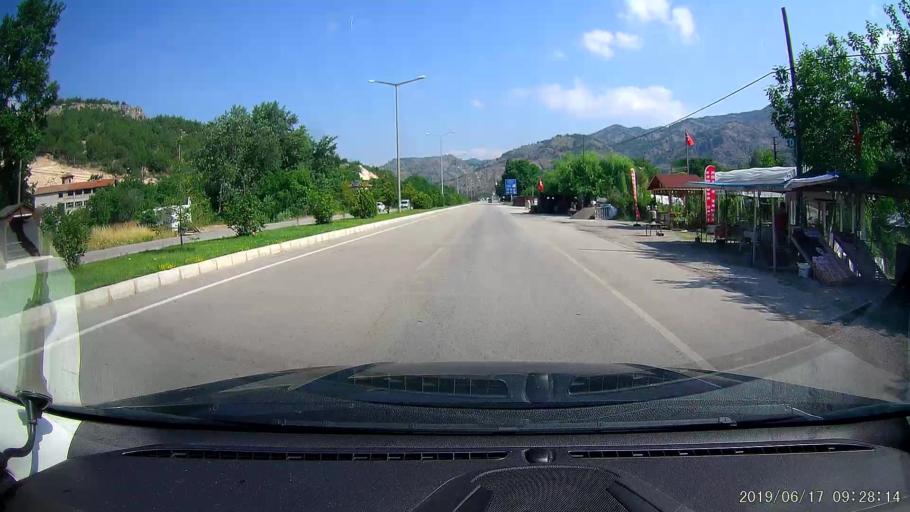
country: TR
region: Amasya
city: Amasya
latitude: 40.6858
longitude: 35.8229
